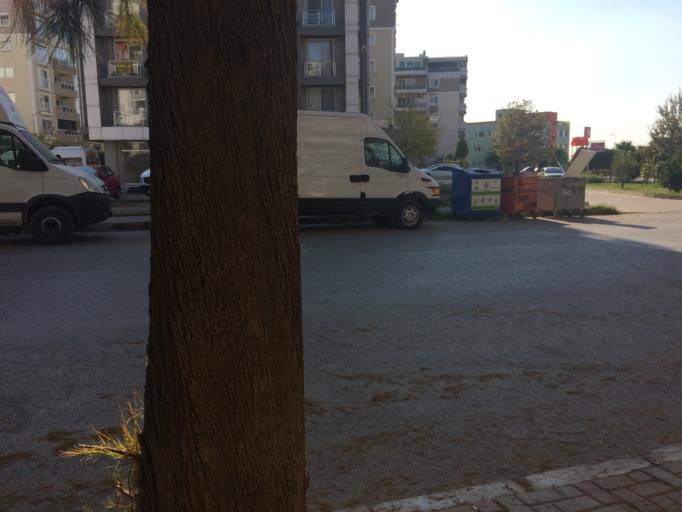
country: TR
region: Izmir
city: Karsiyaka
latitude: 38.4926
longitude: 27.0539
